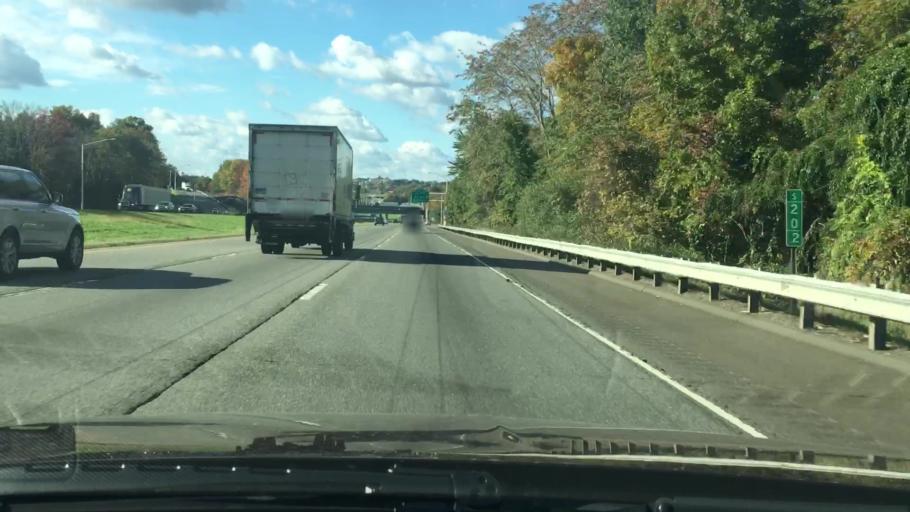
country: US
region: Connecticut
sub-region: New Haven County
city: Meriden
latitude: 41.5413
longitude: -72.7567
